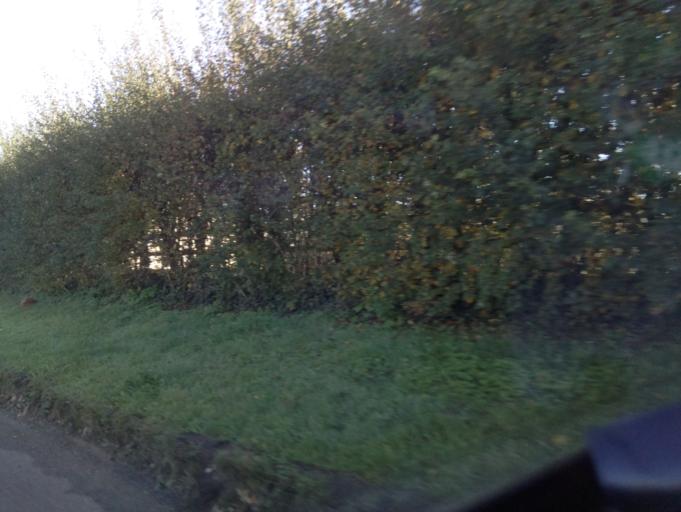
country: GB
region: England
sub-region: Somerset
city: Yeovil
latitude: 50.9205
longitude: -2.6166
